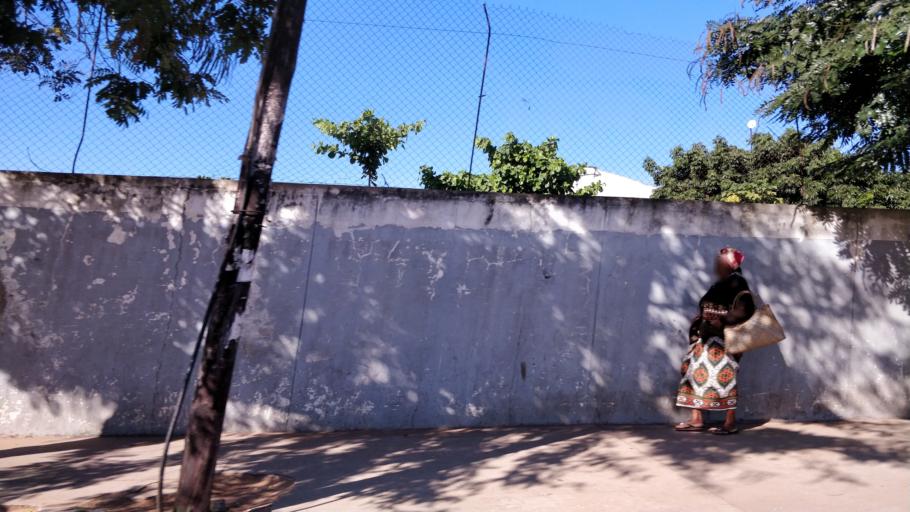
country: MZ
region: Maputo City
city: Maputo
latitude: -25.9282
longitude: 32.6004
